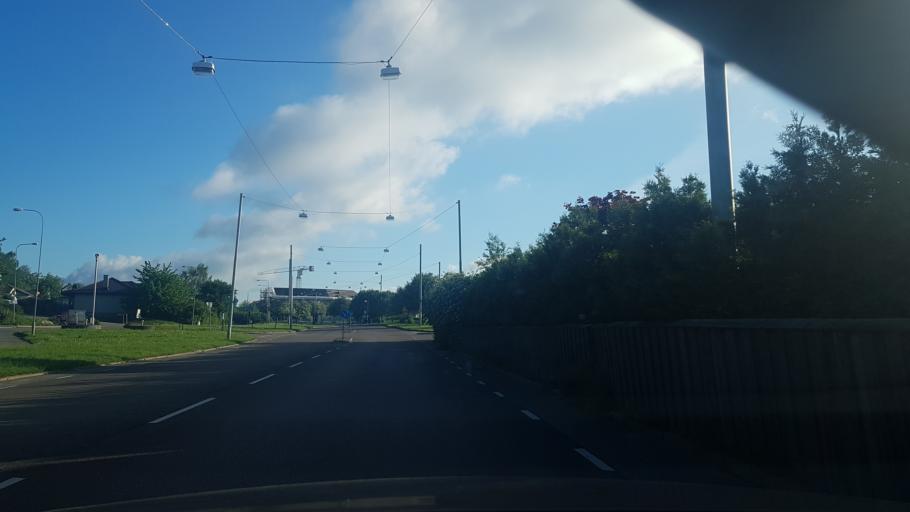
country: SE
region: Vaestra Goetaland
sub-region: Goteborg
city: Majorna
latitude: 57.6378
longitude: 11.8807
